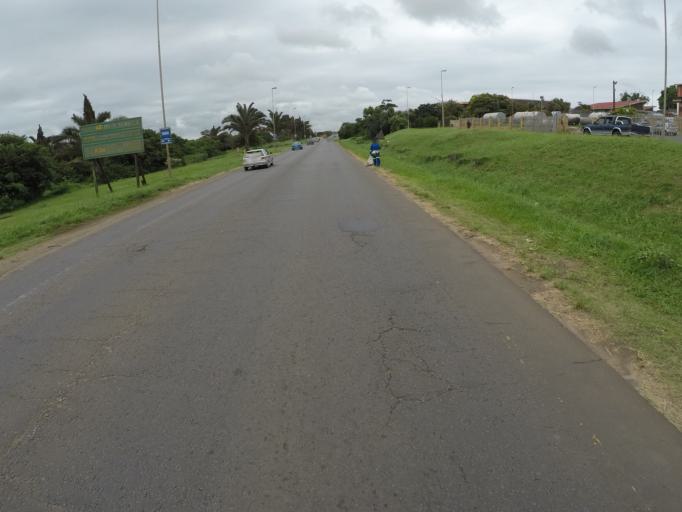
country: ZA
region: KwaZulu-Natal
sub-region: uThungulu District Municipality
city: Empangeni
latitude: -28.7672
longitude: 31.9051
